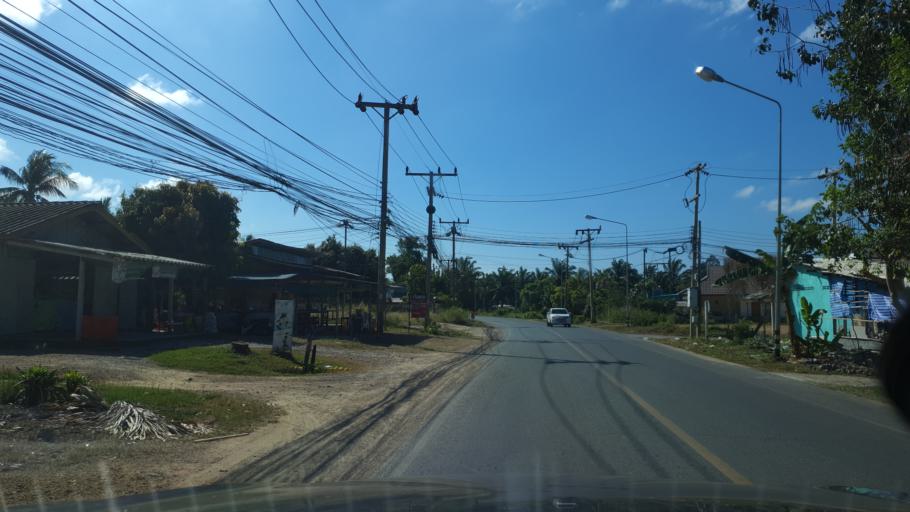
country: TH
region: Phangnga
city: Ban Ao Nang
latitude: 8.0581
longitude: 98.8144
